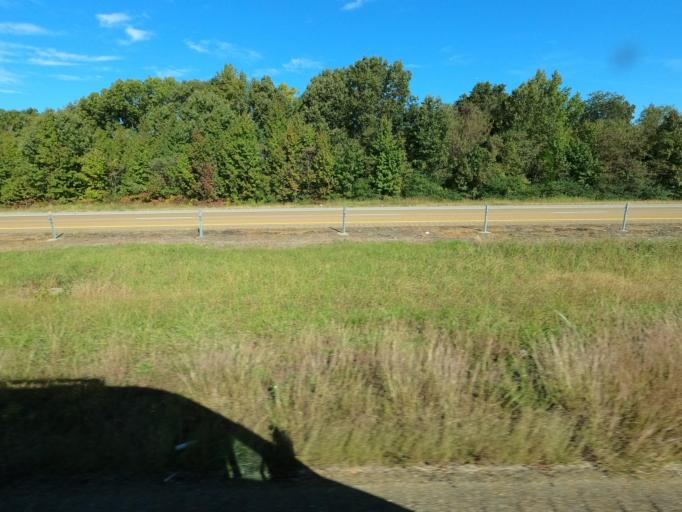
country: US
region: Tennessee
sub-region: Shelby County
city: Lakeland
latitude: 35.3083
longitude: -89.7891
